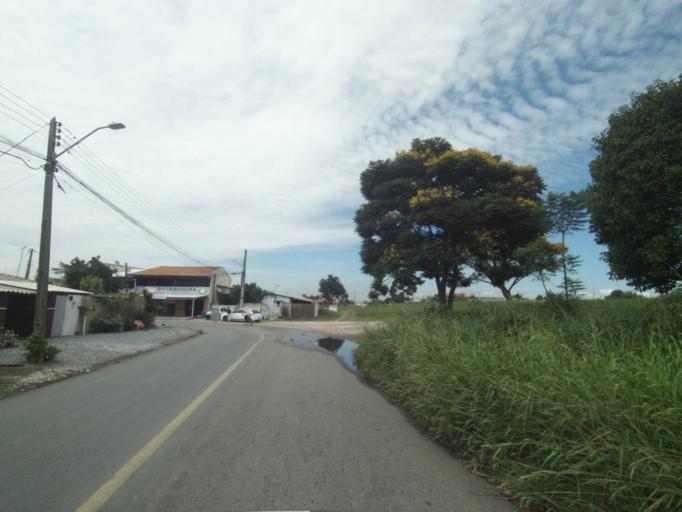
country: BR
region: Parana
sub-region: Pinhais
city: Pinhais
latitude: -25.4738
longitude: -49.1984
